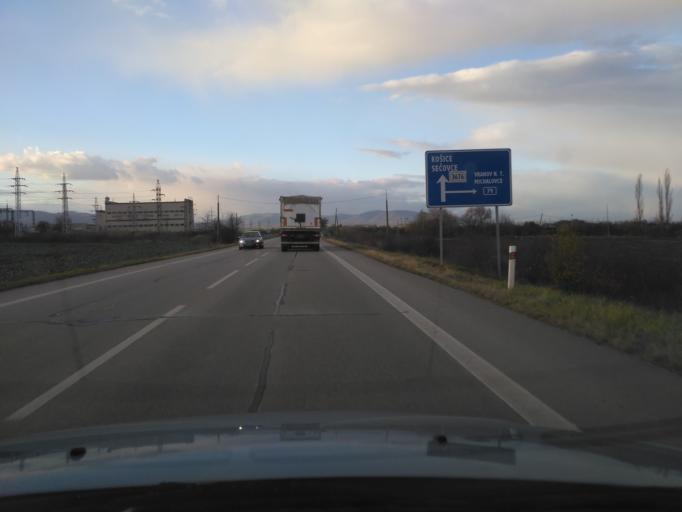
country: SK
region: Kosicky
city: Trebisov
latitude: 48.6294
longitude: 21.6942
